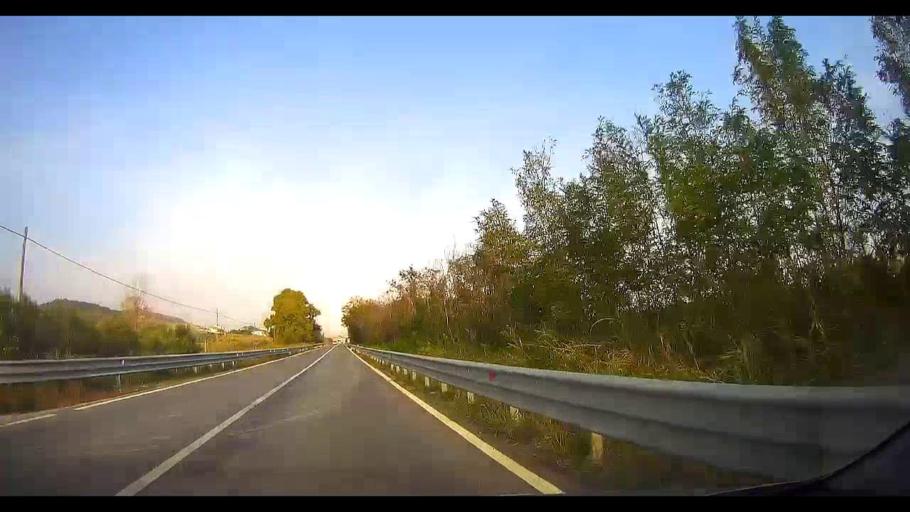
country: IT
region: Calabria
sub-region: Provincia di Cosenza
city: Cariati
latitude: 39.5210
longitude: 16.9023
